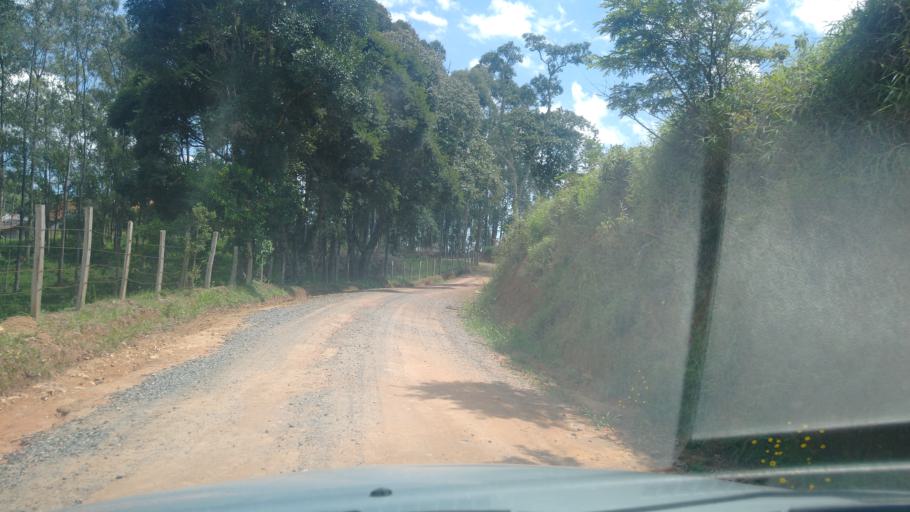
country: BR
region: Minas Gerais
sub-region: Extrema
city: Extrema
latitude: -22.7381
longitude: -46.2953
